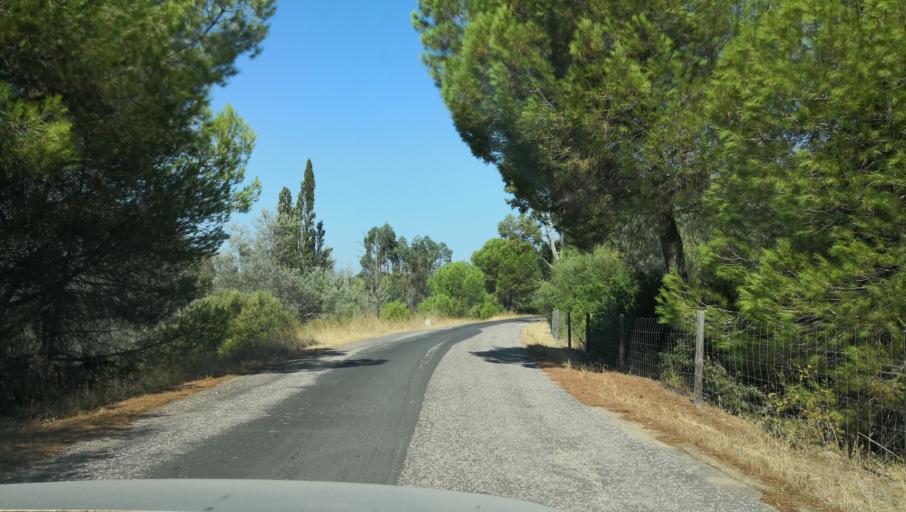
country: PT
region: Setubal
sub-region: Alcacer do Sal
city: Alcacer do Sal
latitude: 38.2498
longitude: -8.2970
